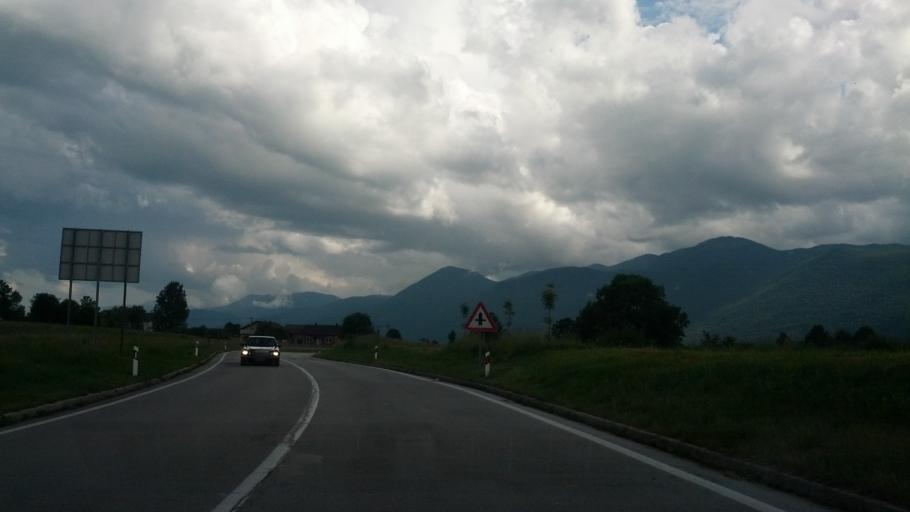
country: BA
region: Federation of Bosnia and Herzegovina
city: Izacic
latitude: 44.8767
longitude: 15.7686
